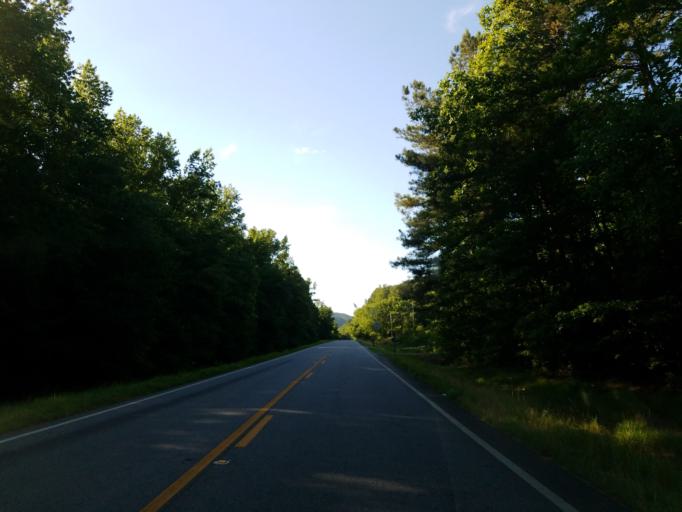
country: US
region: Georgia
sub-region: Gordon County
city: Calhoun
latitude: 34.6258
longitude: -85.0566
